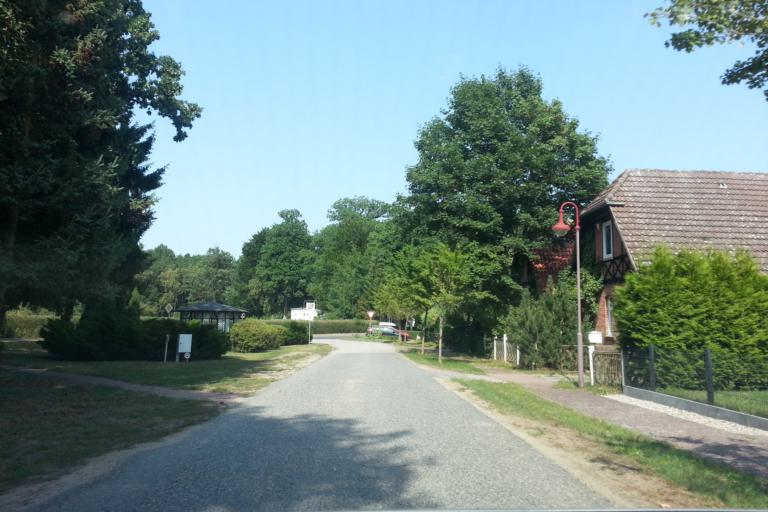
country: DE
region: Mecklenburg-Vorpommern
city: Ferdinandshof
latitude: 53.5951
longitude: 13.8271
